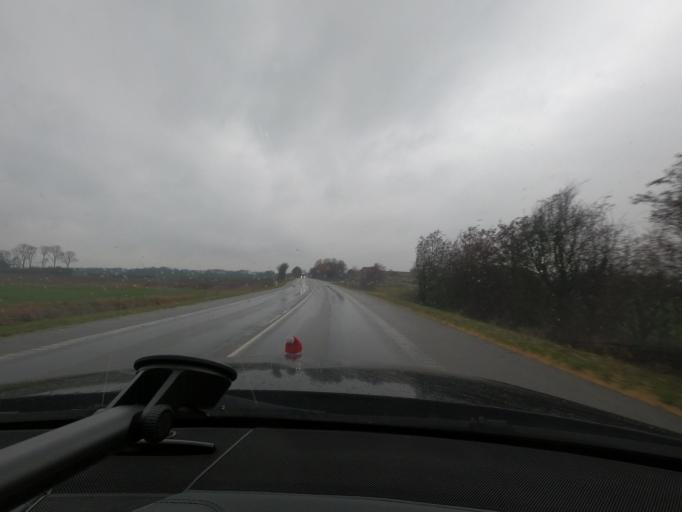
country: DK
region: South Denmark
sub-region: Sonderborg Kommune
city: Horuphav
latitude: 54.8942
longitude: 9.9682
